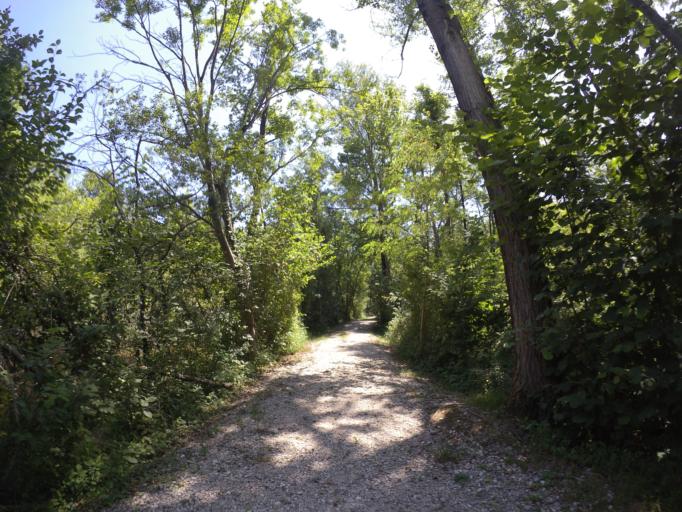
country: IT
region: Friuli Venezia Giulia
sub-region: Provincia di Udine
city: Bertiolo
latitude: 45.9173
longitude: 13.0755
